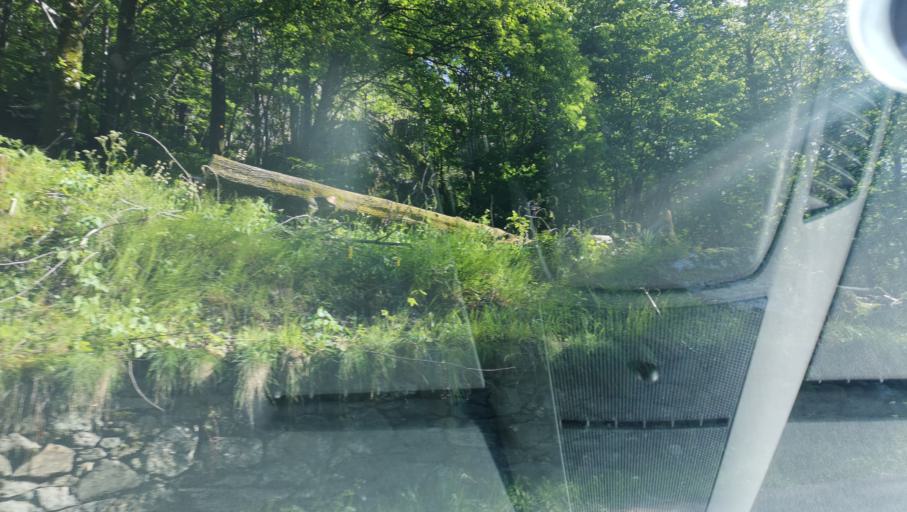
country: IT
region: Piedmont
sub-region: Provincia di Torino
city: Usseglio
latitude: 45.2152
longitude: 7.1812
